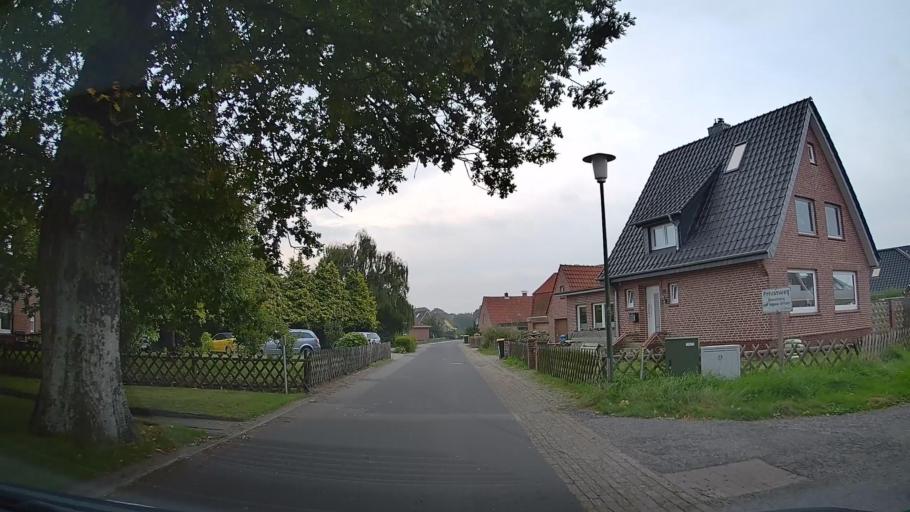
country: DE
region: Lower Saxony
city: Wanna
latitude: 53.8283
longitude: 8.7663
